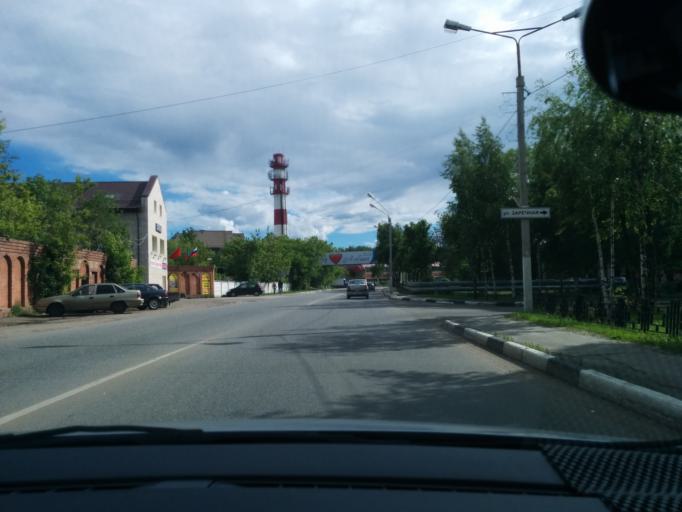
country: RU
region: Moskovskaya
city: Lobnya
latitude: 56.0184
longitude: 37.4724
